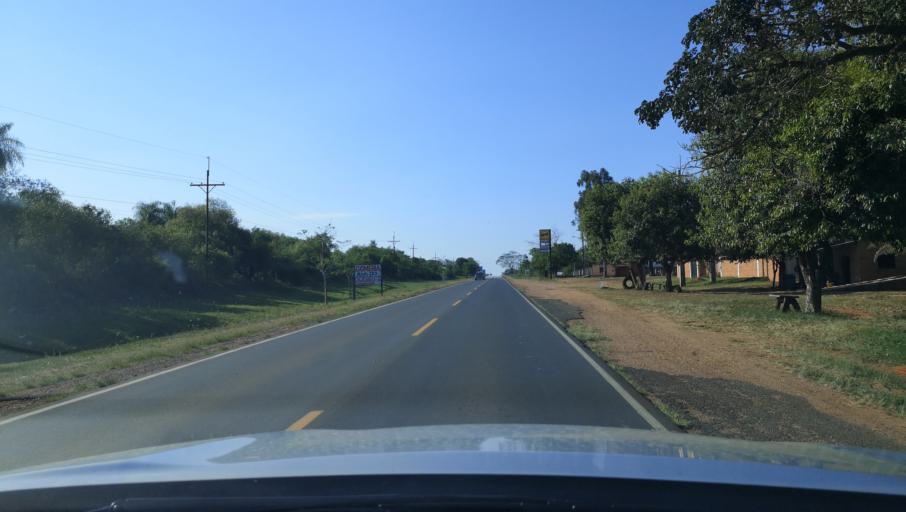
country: PY
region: Misiones
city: Santa Maria
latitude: -26.8641
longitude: -57.0337
